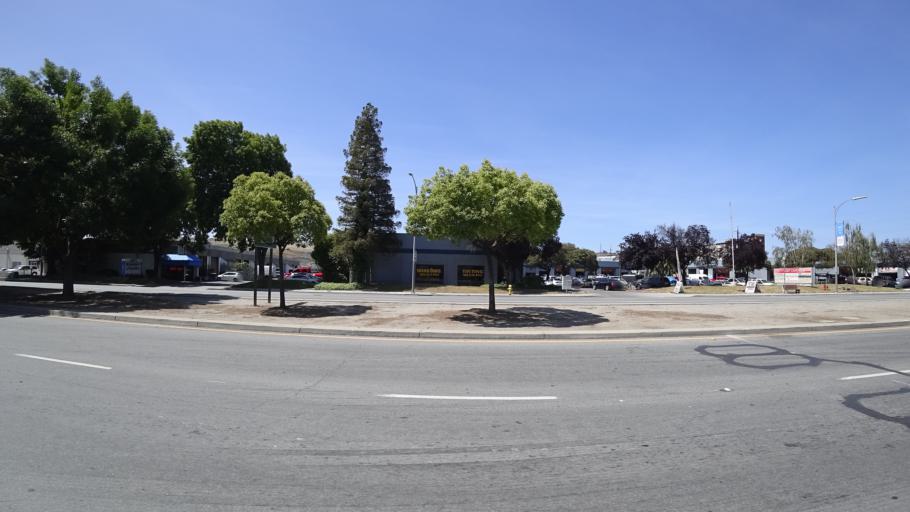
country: US
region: California
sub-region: Santa Clara County
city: Seven Trees
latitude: 37.2919
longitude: -121.8495
